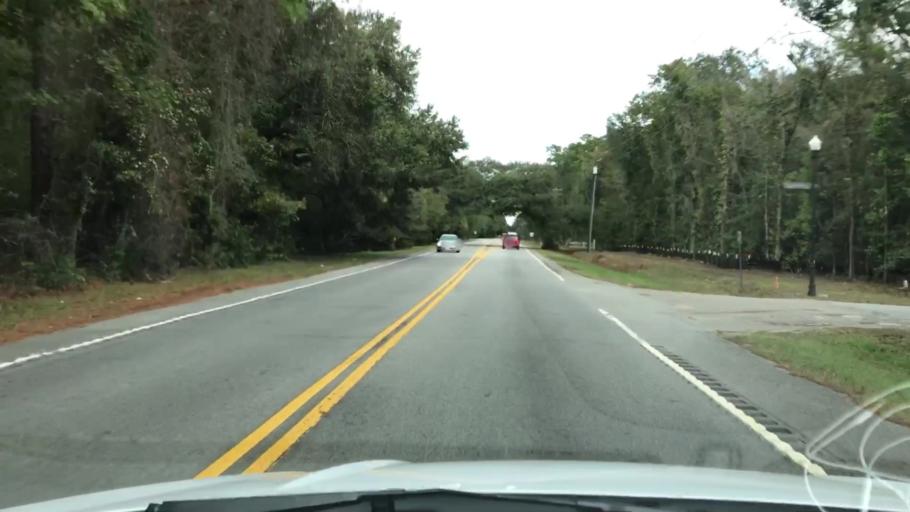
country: US
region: South Carolina
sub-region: Beaufort County
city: Bluffton
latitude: 32.2309
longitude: -80.9085
